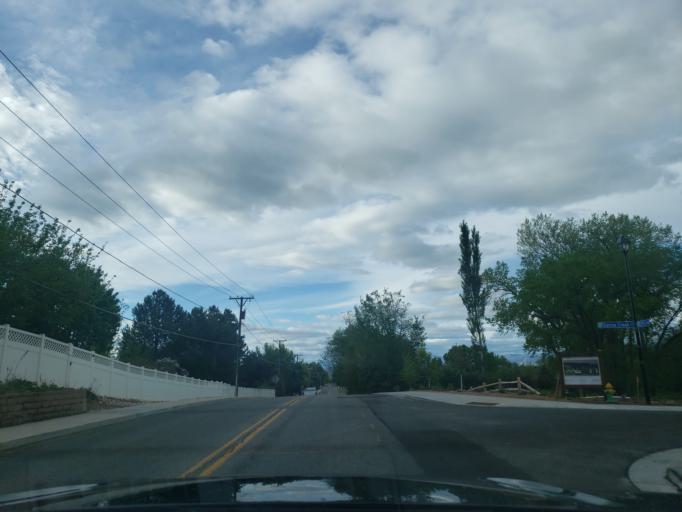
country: US
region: Colorado
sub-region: Mesa County
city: Redlands
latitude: 39.0962
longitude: -108.6687
